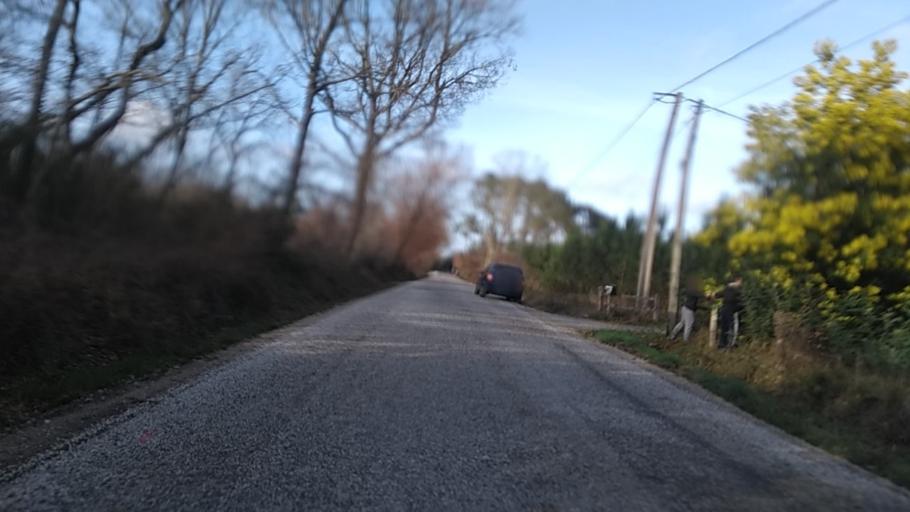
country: FR
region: Aquitaine
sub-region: Departement de la Gironde
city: Le Barp
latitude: 44.5823
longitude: -0.7706
